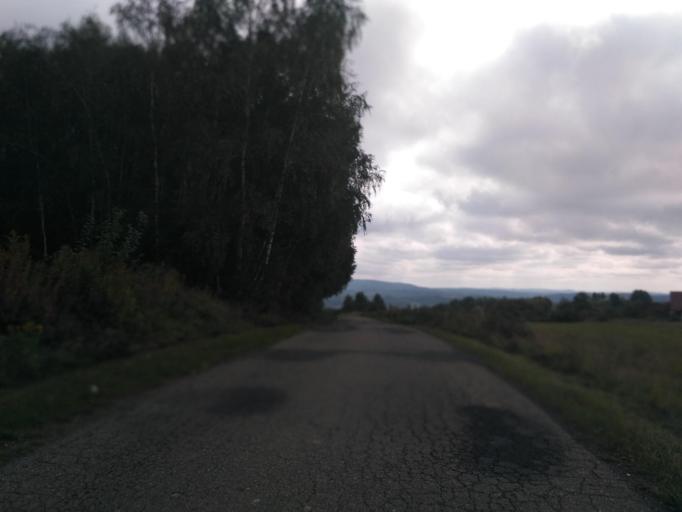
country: PL
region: Subcarpathian Voivodeship
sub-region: Powiat ropczycko-sedziszowski
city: Niedzwiada
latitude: 49.9504
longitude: 21.4602
